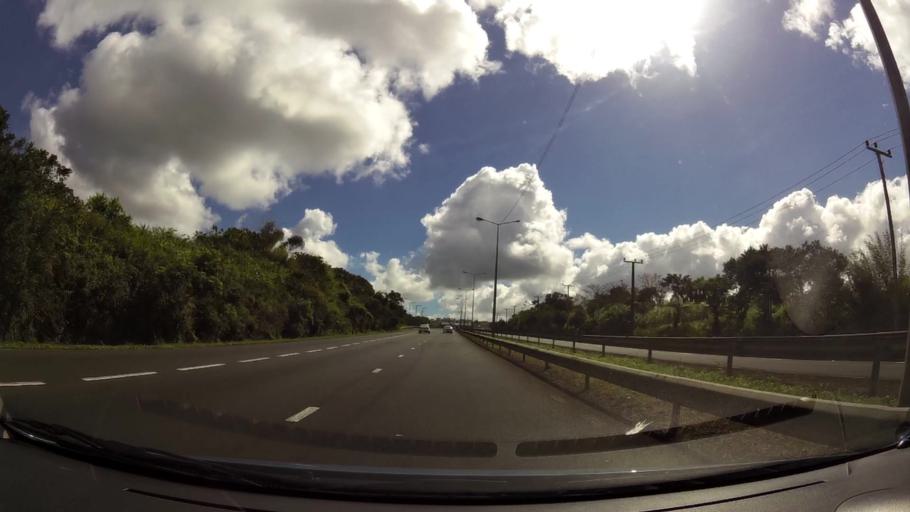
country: MU
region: Grand Port
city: Rose Belle
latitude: -20.3925
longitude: 57.5765
